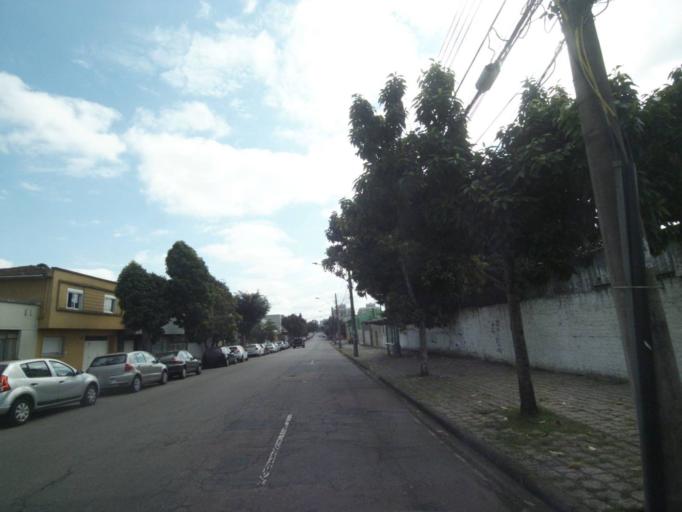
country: BR
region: Parana
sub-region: Curitiba
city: Curitiba
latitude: -25.4470
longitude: -49.2613
